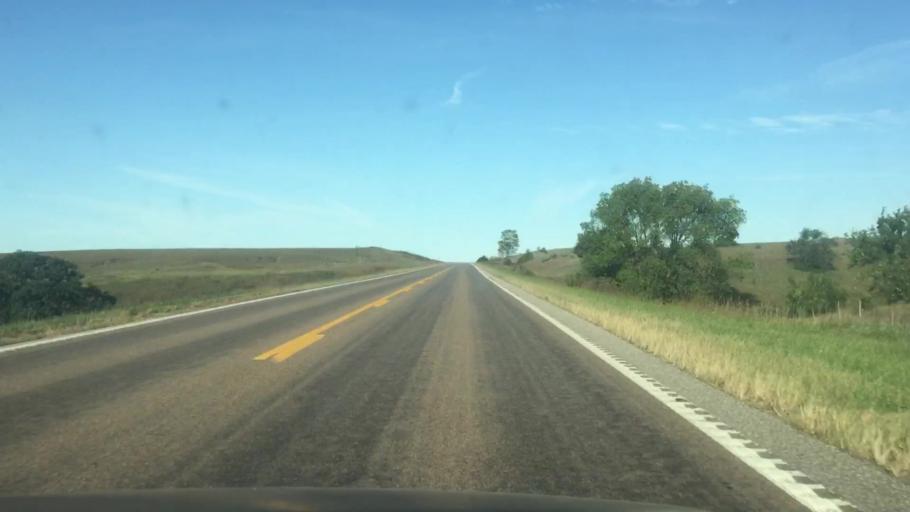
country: US
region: Nebraska
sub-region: Thayer County
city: Hebron
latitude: 40.1473
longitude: -97.5238
